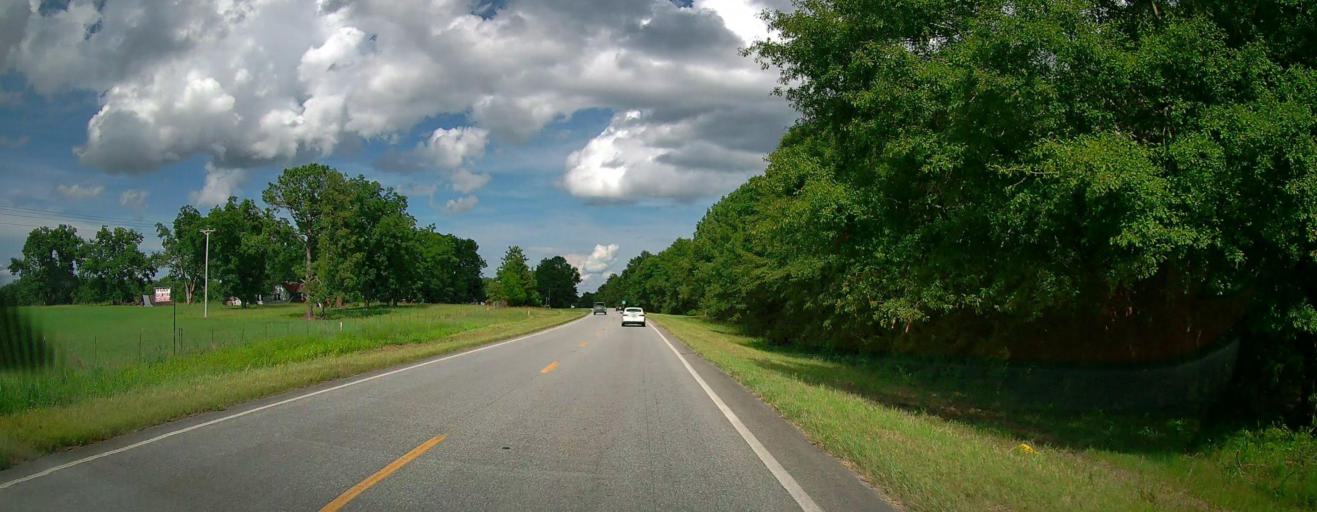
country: US
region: Alabama
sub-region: Lee County
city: Opelika
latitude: 32.4410
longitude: -85.2998
